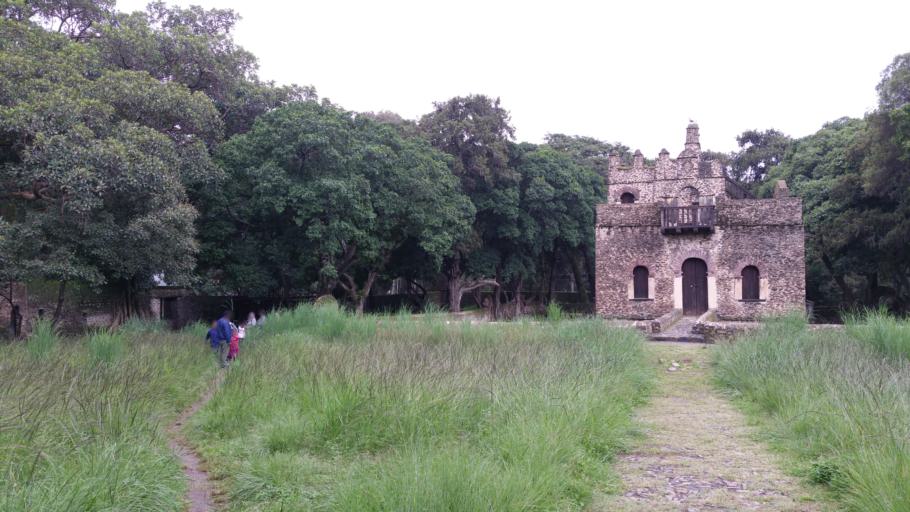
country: ET
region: Amhara
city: Gondar
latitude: 12.6177
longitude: 37.4570
